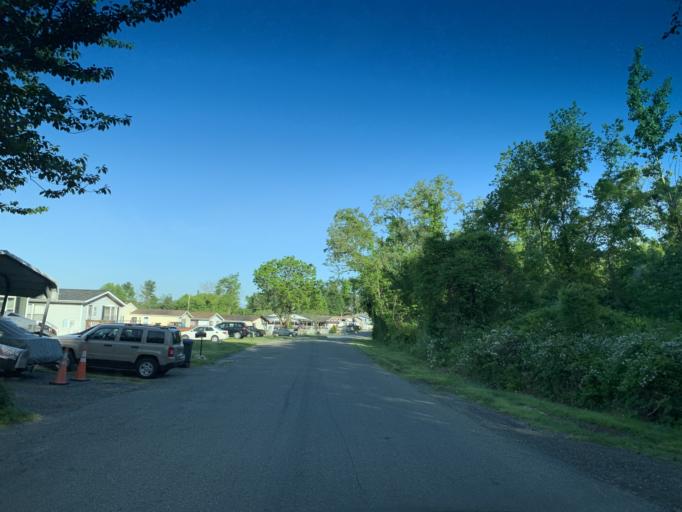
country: US
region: Maryland
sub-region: Harford County
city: Riverside
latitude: 39.4619
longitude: -76.2629
